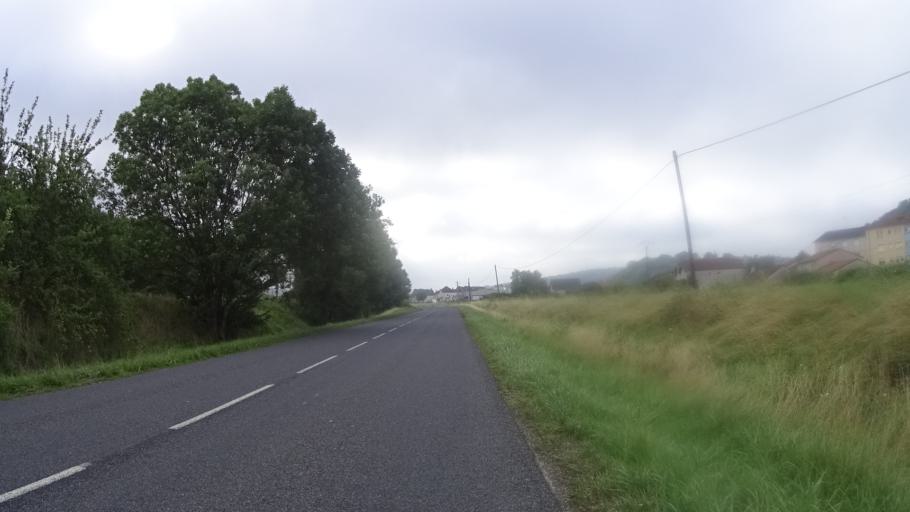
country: FR
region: Lorraine
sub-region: Departement de la Meuse
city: Fains-Veel
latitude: 48.7947
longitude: 5.1206
